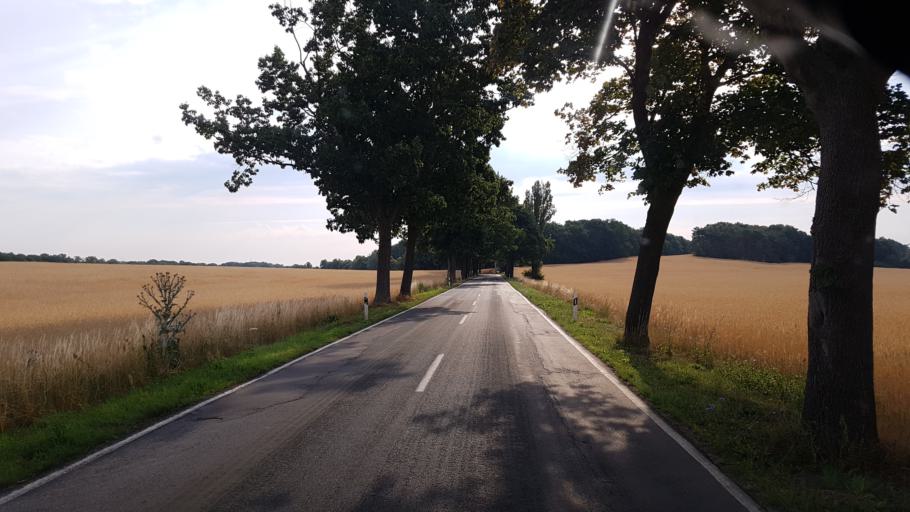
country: DE
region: Brandenburg
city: Golssen
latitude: 51.9662
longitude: 13.5473
